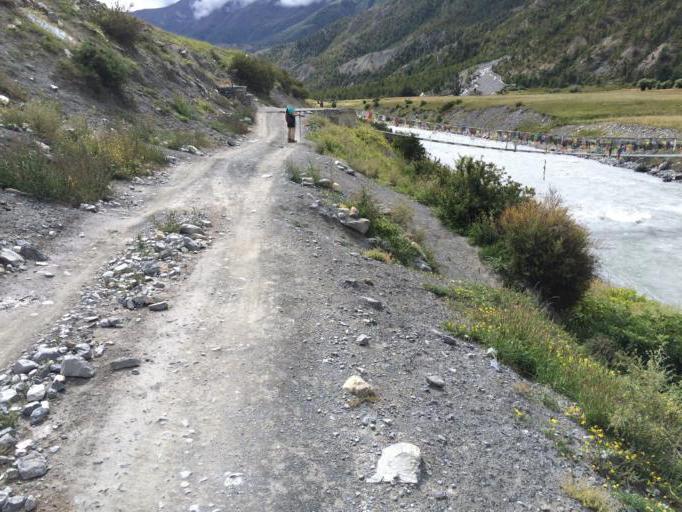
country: NP
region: Western Region
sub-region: Gandaki Zone
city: Nawal
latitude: 28.6548
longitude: 84.0424
